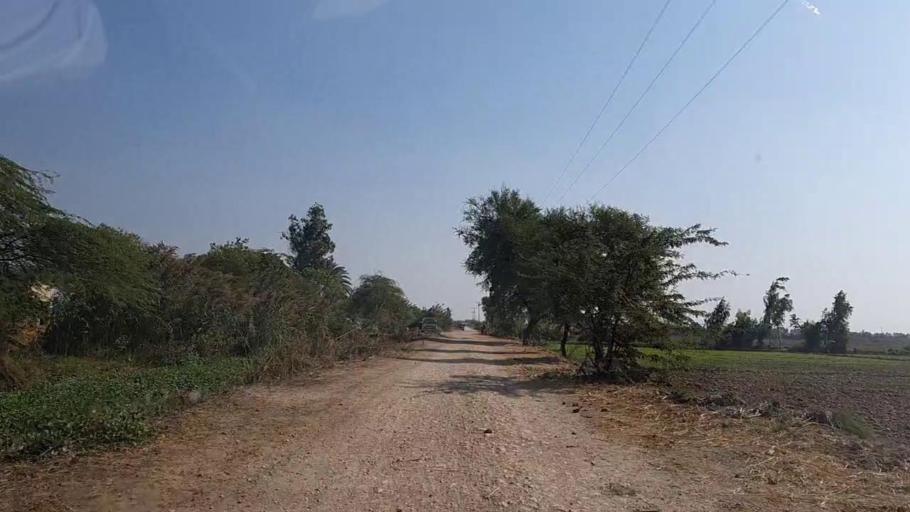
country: PK
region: Sindh
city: Thatta
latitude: 24.7976
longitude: 67.9733
